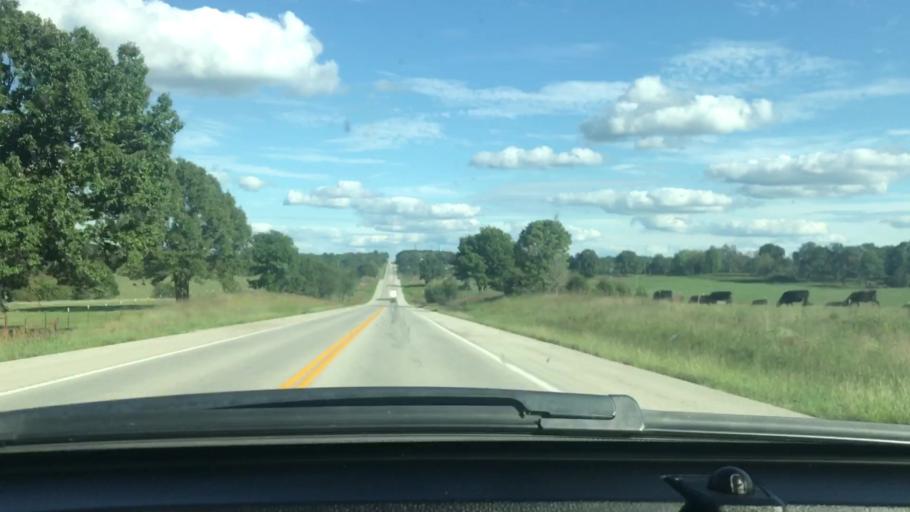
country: US
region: Missouri
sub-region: Howell County
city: West Plains
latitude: 36.6591
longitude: -91.7055
